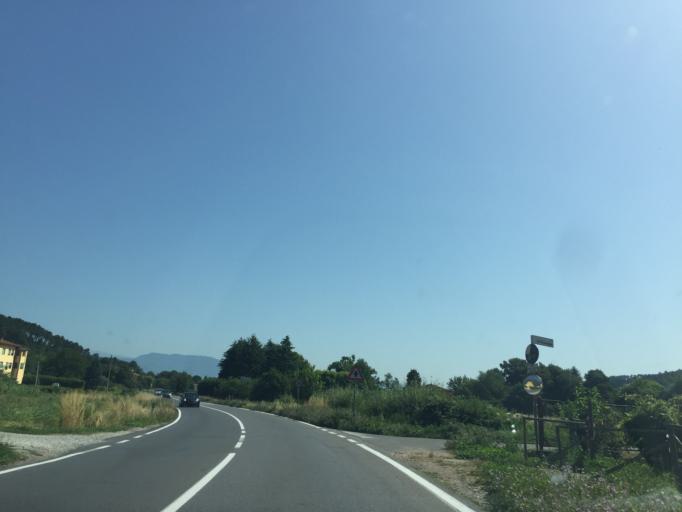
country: IT
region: Tuscany
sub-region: Province of Pisa
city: Asciano
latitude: 43.7900
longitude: 10.4746
